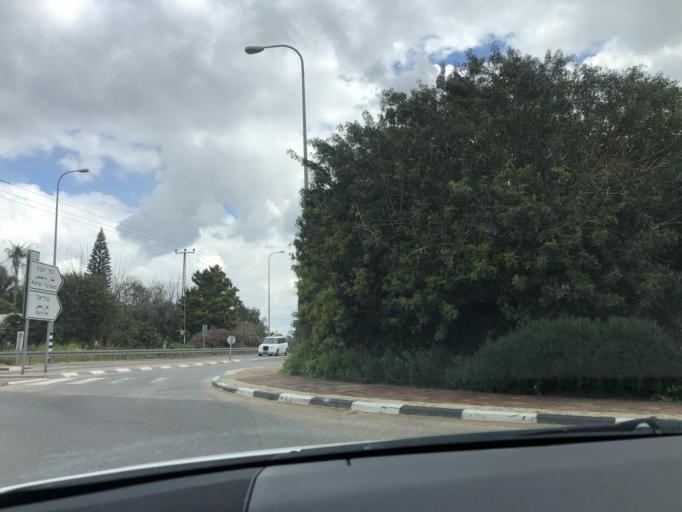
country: IL
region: Central District
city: Tel Mond
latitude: 32.2609
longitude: 34.9300
